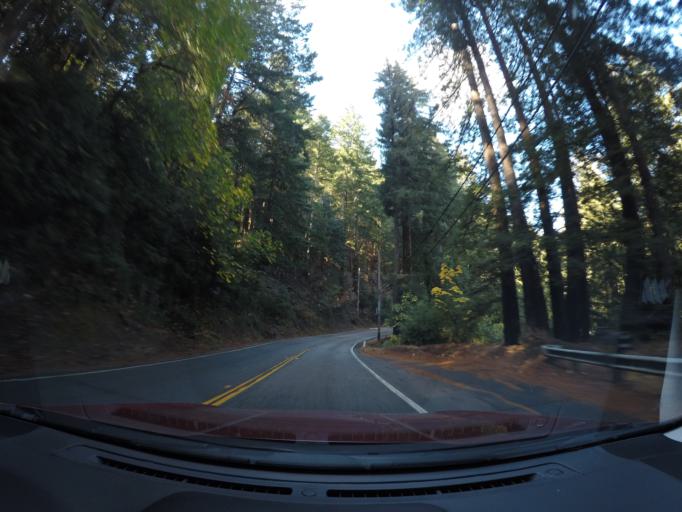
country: US
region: California
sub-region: Santa Cruz County
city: Brookdale
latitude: 37.1132
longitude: -122.1171
